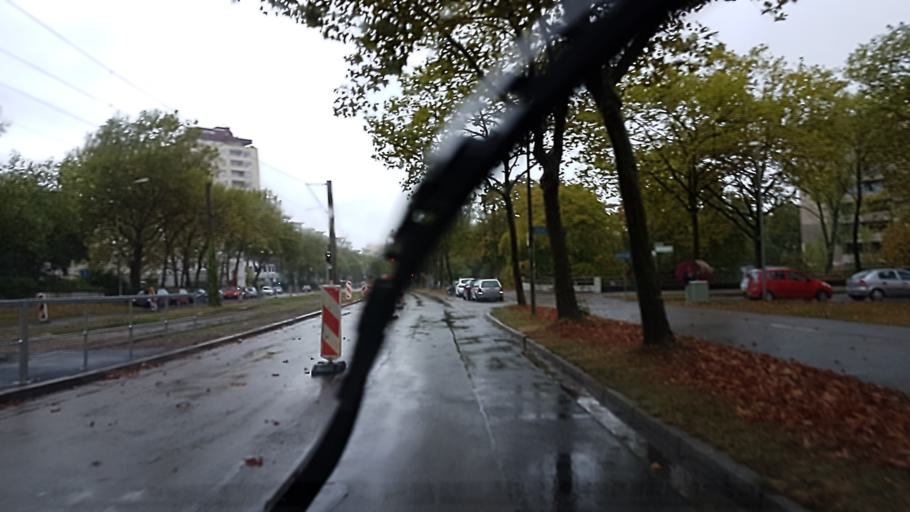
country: DE
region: Baden-Wuerttemberg
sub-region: Freiburg Region
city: Freiburg
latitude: 48.0059
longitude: 7.8209
